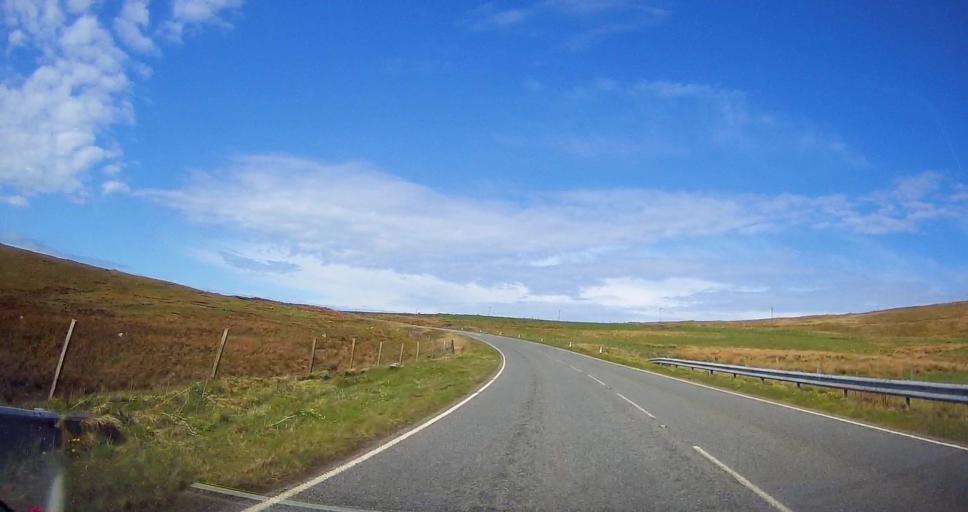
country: GB
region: Scotland
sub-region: Shetland Islands
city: Sandwick
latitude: 60.0105
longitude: -1.2583
